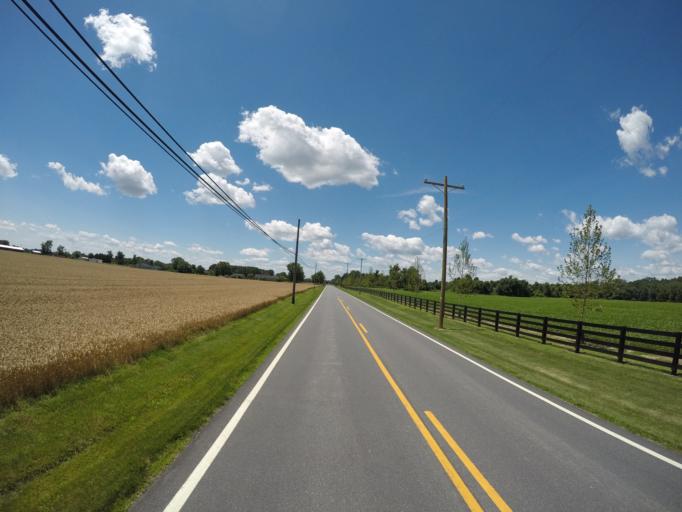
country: US
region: Delaware
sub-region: New Castle County
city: Middletown
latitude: 39.4616
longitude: -75.7546
